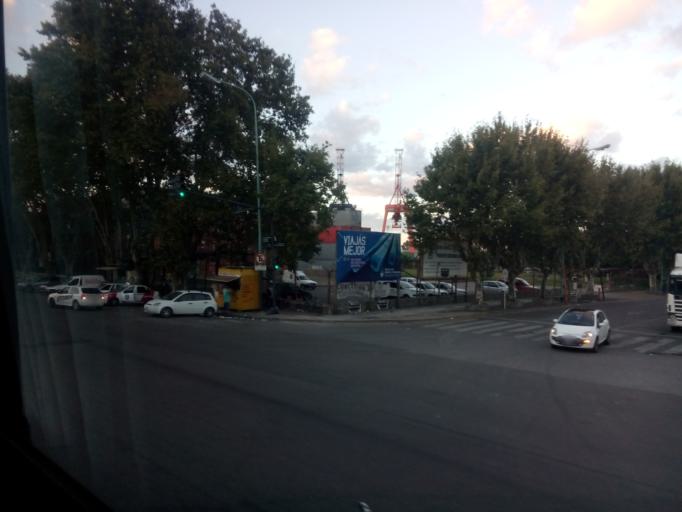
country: AR
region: Buenos Aires F.D.
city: Retiro
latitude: -34.5804
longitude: -58.3750
